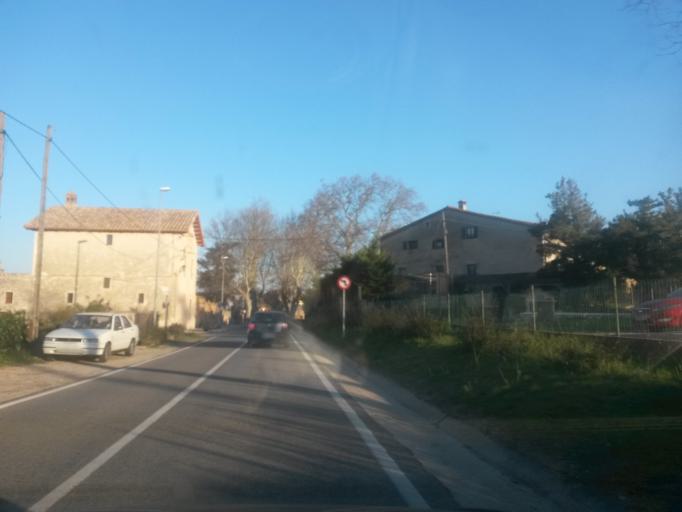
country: ES
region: Catalonia
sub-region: Provincia de Girona
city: Darnius
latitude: 42.3662
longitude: 2.8324
